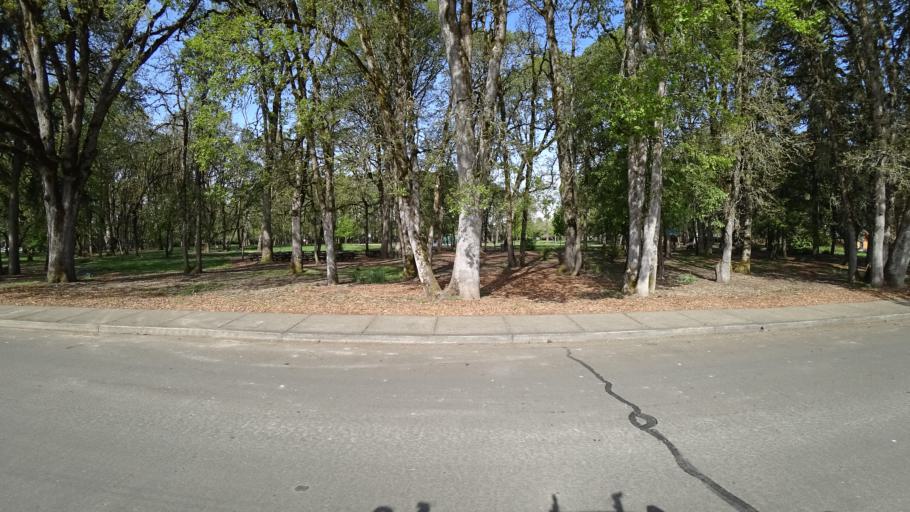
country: US
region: Oregon
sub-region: Washington County
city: Hillsboro
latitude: 45.5265
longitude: -122.9585
